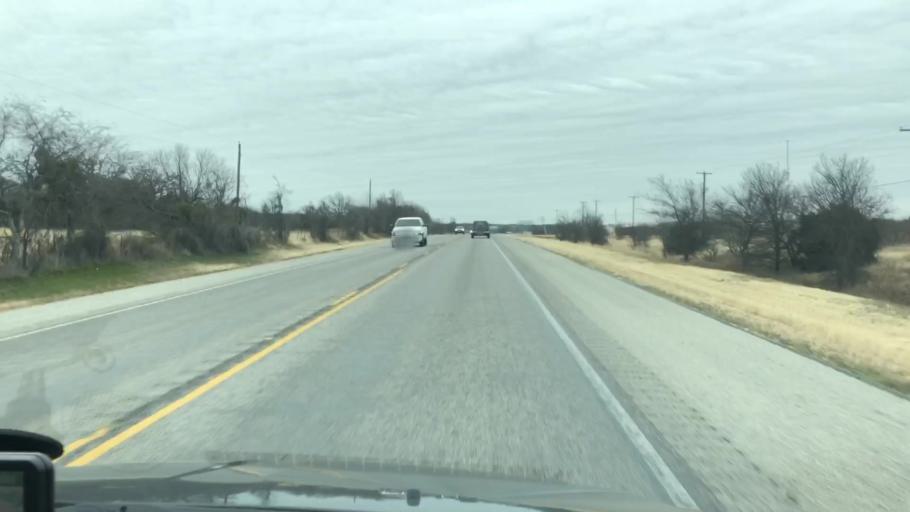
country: US
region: Texas
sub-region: Palo Pinto County
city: Mineral Wells
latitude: 32.8470
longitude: -98.0999
